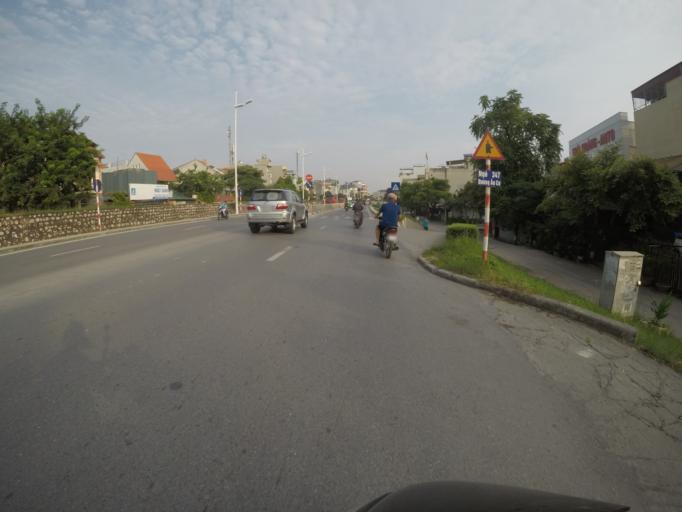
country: VN
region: Ha Noi
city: Tay Ho
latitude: 21.0742
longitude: 105.8241
